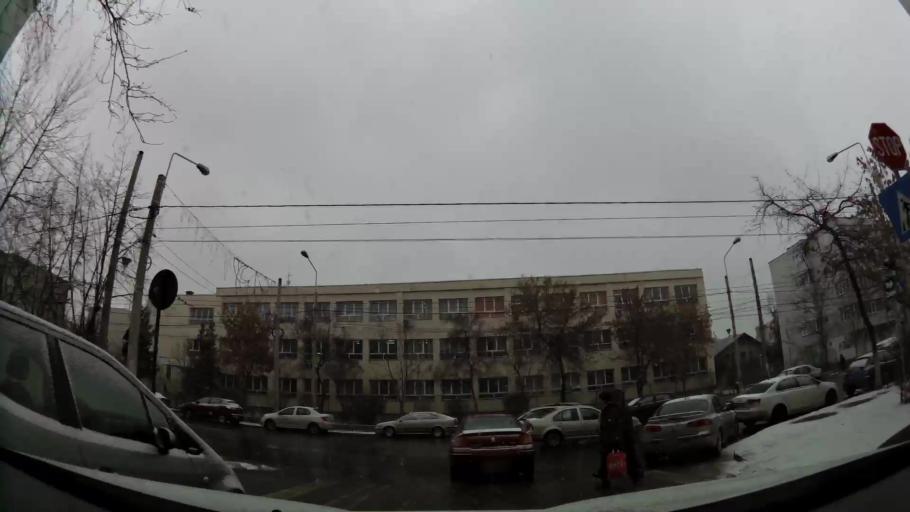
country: RO
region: Prahova
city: Ploiesti
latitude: 44.9416
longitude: 26.0003
